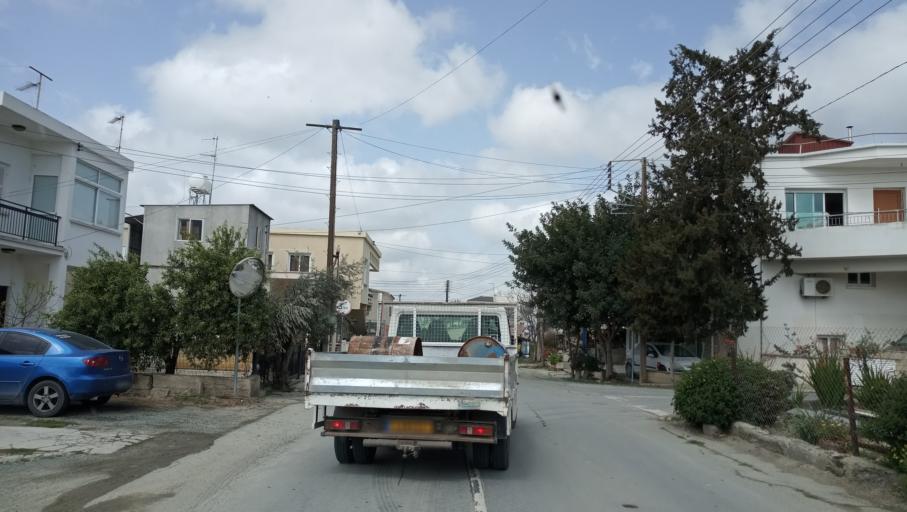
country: CY
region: Lefkosia
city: Dali
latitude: 35.0249
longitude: 33.4257
